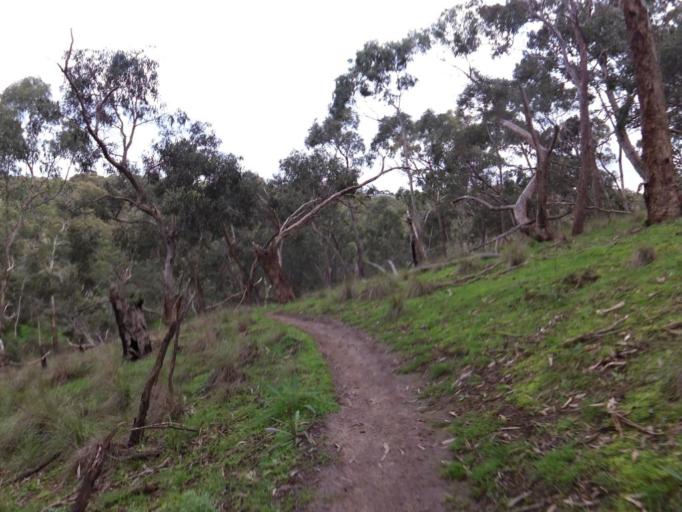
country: AU
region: Victoria
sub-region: Banyule
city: Watsonia North
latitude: -37.6795
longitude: 145.0880
